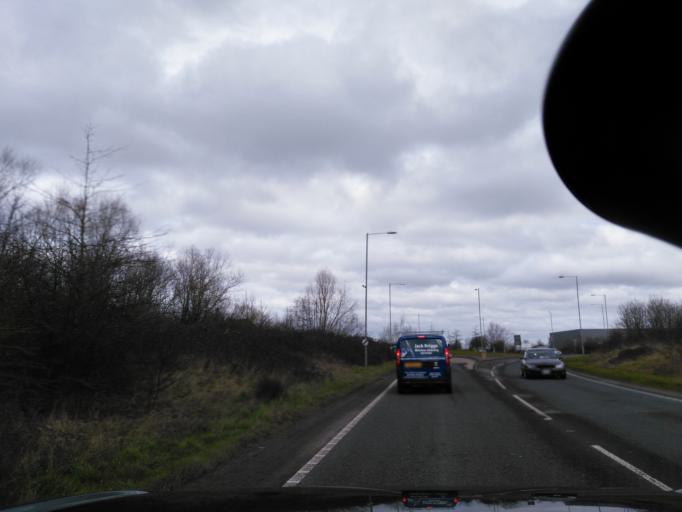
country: GB
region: England
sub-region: Wiltshire
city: Melksham
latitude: 51.3535
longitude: -2.1381
